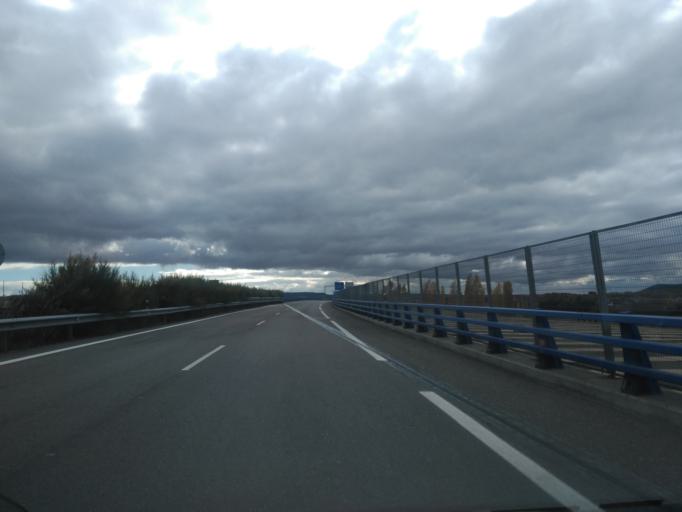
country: ES
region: Castille and Leon
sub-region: Provincia de Palencia
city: Villamuriel de Cerrato
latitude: 41.9608
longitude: -4.5033
